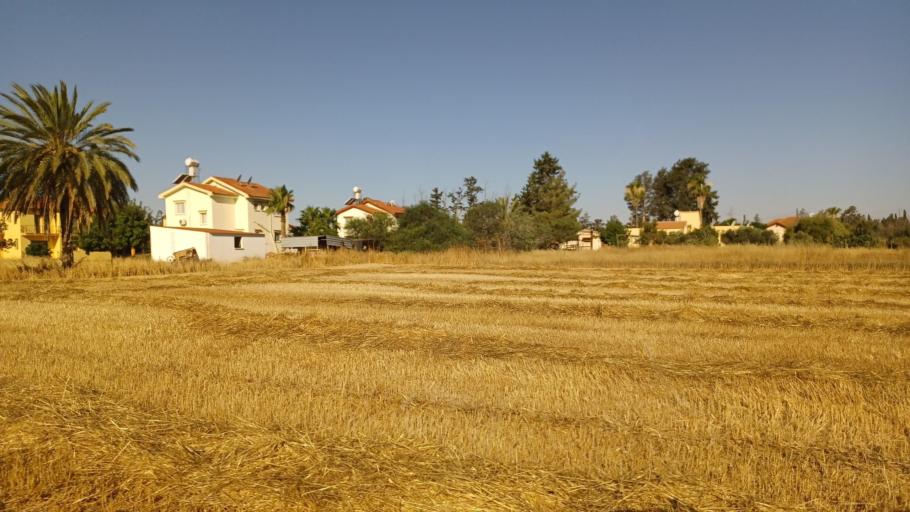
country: CY
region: Larnaka
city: Pergamos
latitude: 35.0357
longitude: 33.7079
